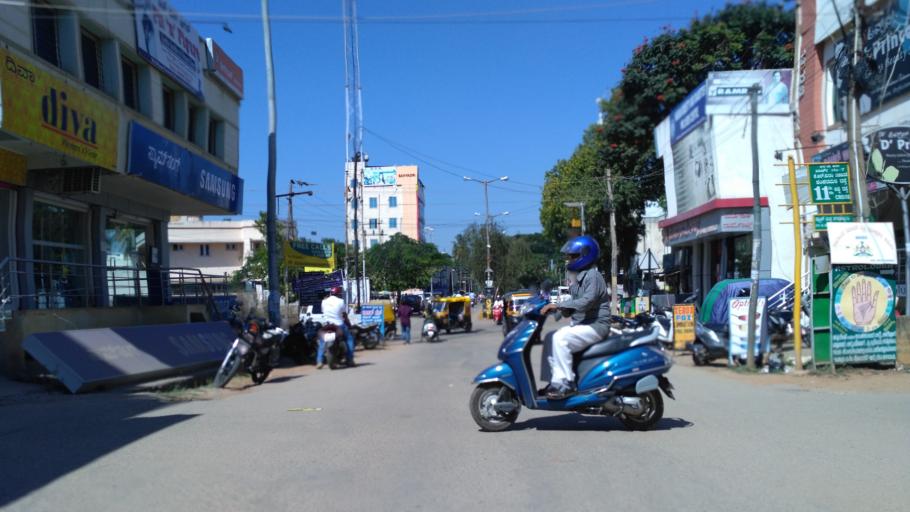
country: IN
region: Karnataka
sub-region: Hassan
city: Hassan
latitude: 13.0107
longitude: 76.1060
